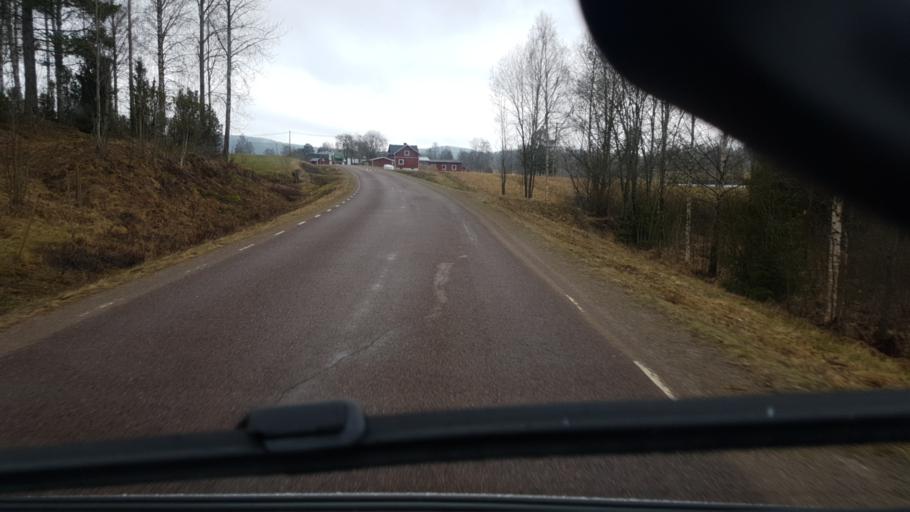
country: SE
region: Vaermland
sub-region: Eda Kommun
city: Charlottenberg
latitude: 59.9699
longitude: 12.4084
